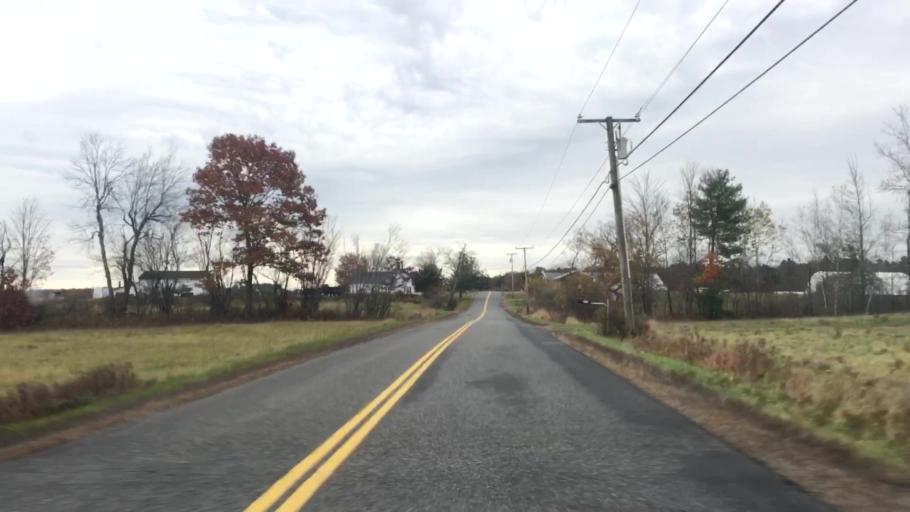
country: US
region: Maine
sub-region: Kennebec County
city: Pittston
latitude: 44.1706
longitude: -69.7226
